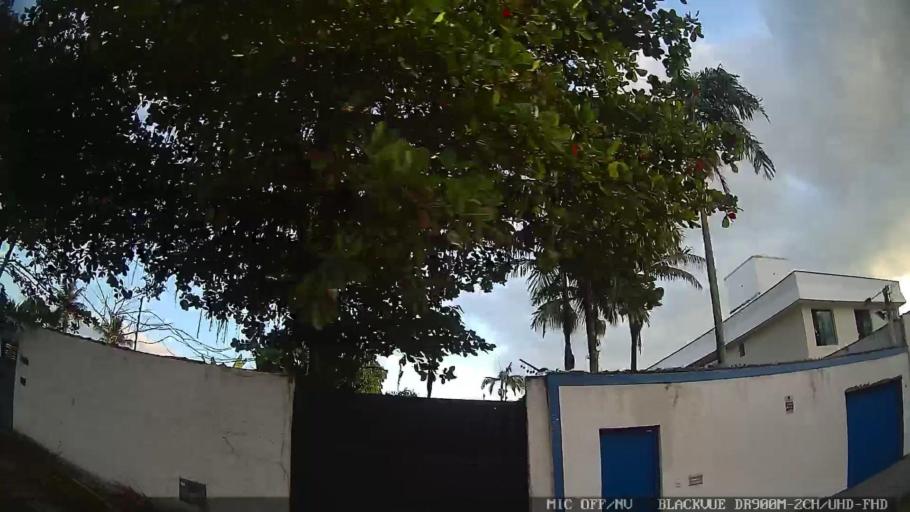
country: BR
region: Sao Paulo
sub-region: Guaruja
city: Guaruja
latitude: -23.9860
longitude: -46.2057
